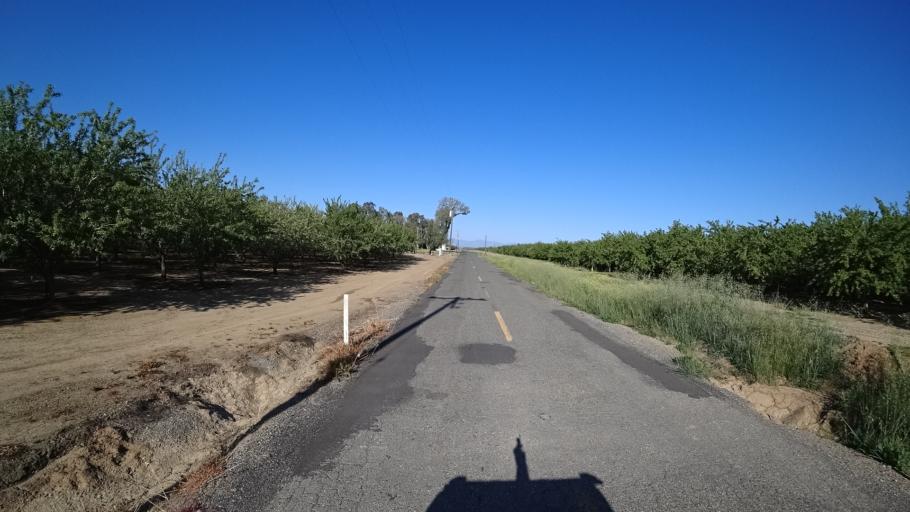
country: US
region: California
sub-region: Glenn County
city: Orland
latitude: 39.6960
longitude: -122.1127
